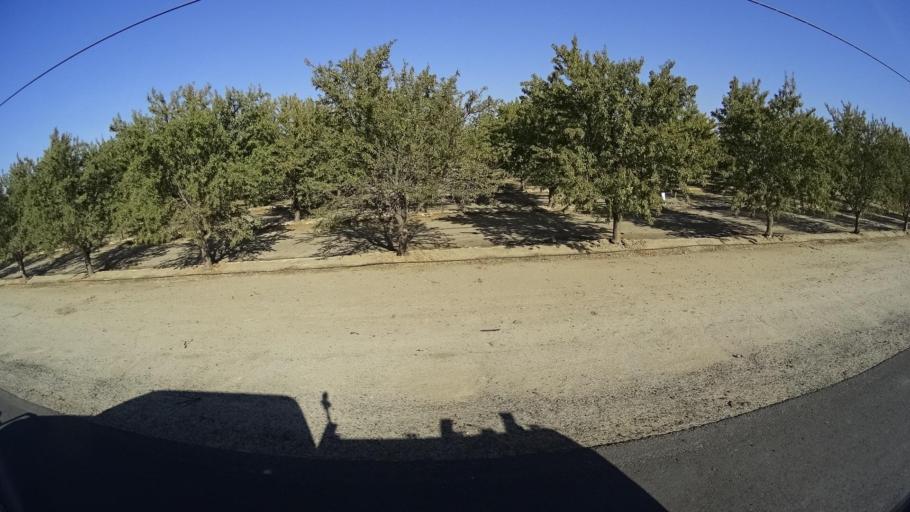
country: US
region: California
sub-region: Kern County
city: Delano
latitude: 35.7178
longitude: -119.3078
